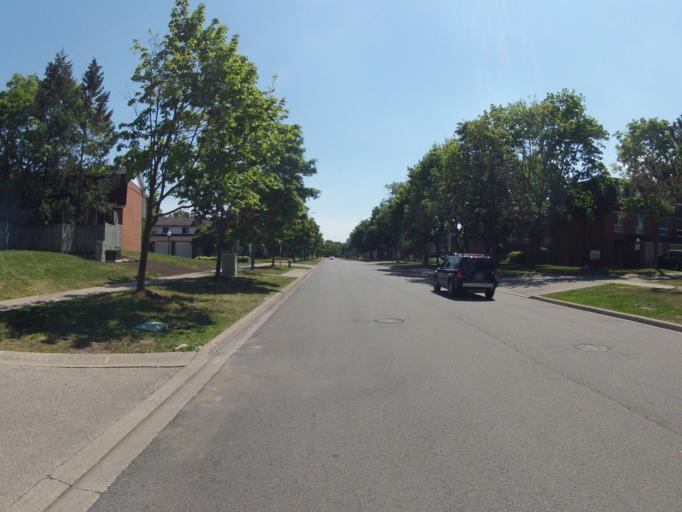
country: CA
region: Ontario
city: Oakville
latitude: 43.5078
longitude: -79.6433
